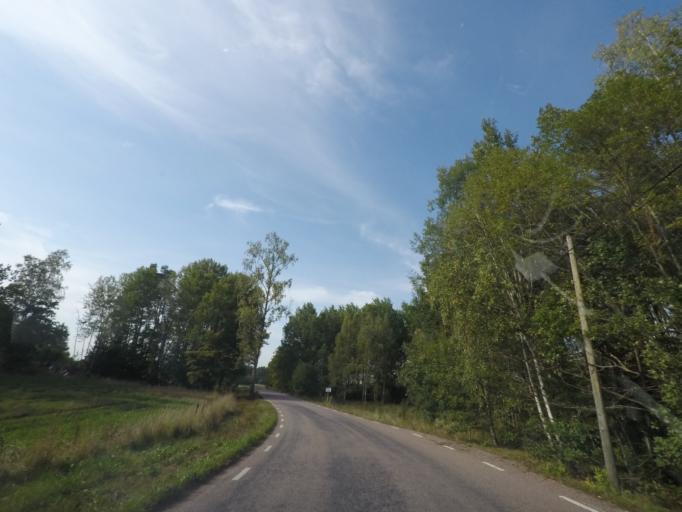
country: SE
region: Vaestmanland
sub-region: Hallstahammars Kommun
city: Kolback
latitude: 59.5287
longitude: 16.1573
